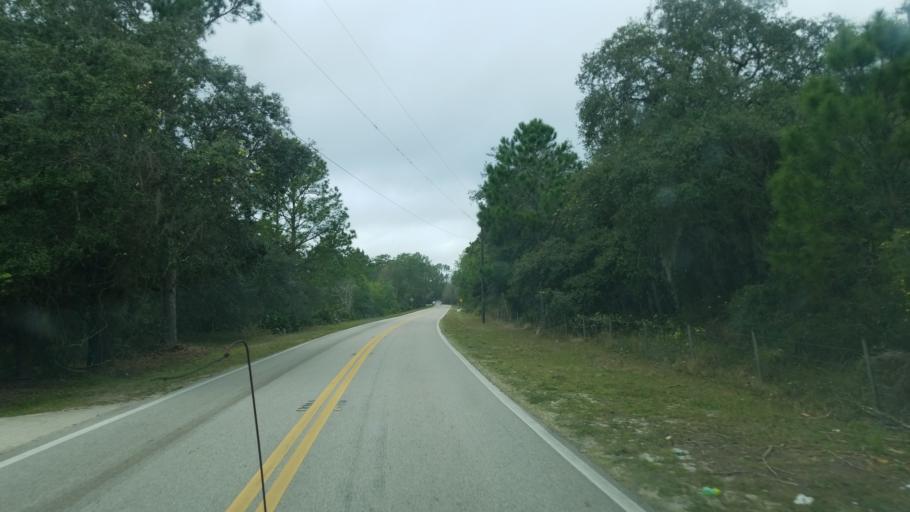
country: US
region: Florida
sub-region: Lake County
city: Four Corners
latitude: 28.2595
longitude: -81.7151
